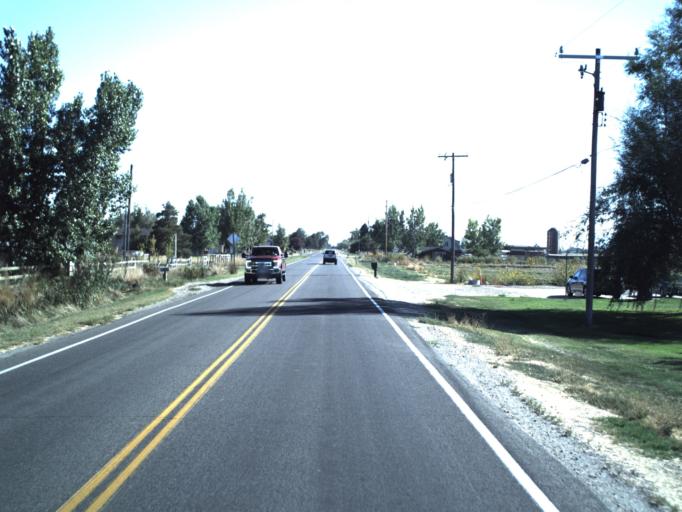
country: US
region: Utah
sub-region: Weber County
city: Hooper
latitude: 41.1886
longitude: -112.1226
